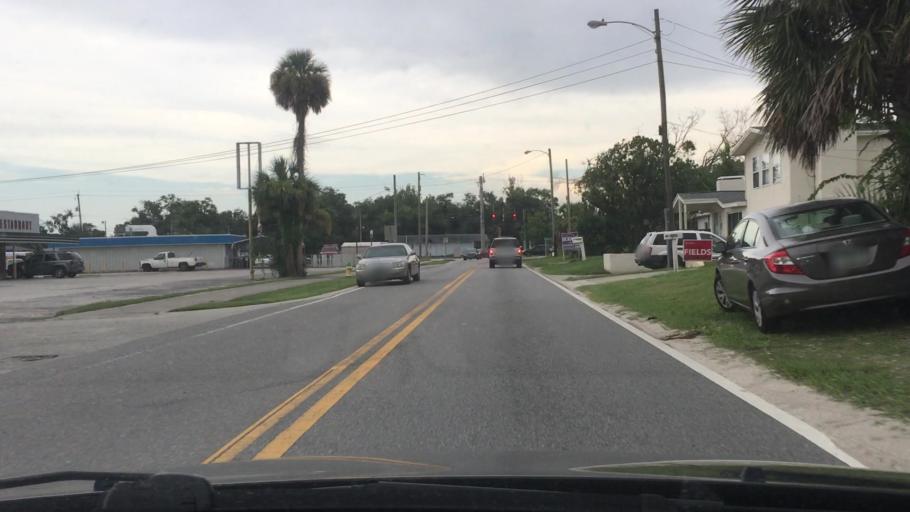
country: US
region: Florida
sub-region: Volusia County
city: Holly Hill
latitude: 29.2173
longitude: -81.0561
